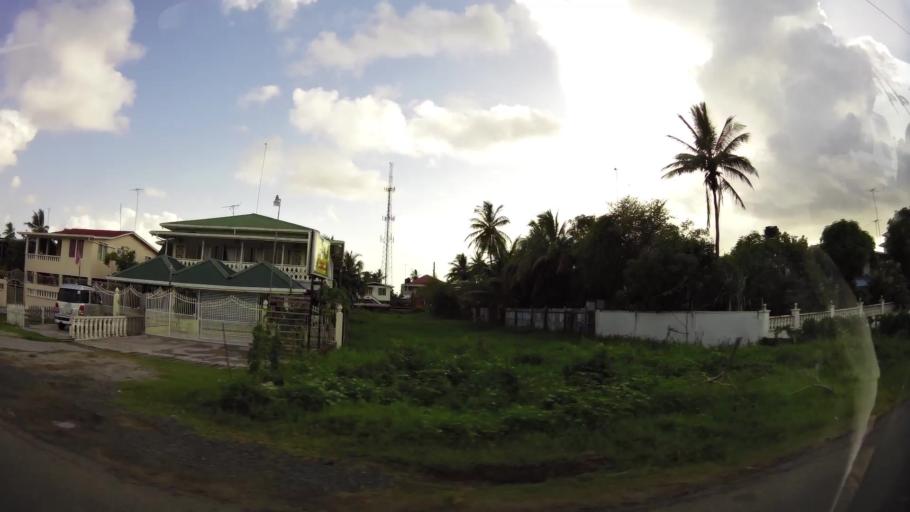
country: GY
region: Demerara-Mahaica
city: Georgetown
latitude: 6.7968
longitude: -58.0359
